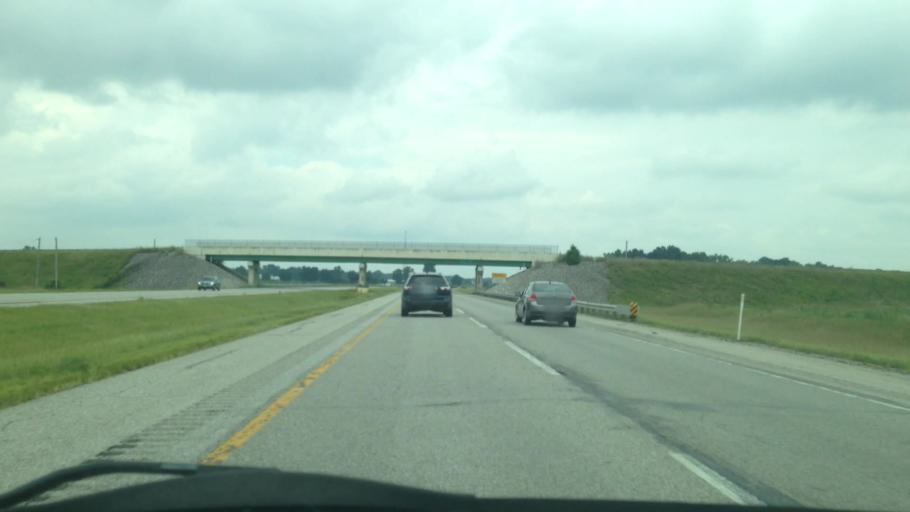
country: US
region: Michigan
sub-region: Saint Joseph County
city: Sturgis
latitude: 41.7481
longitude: -85.4988
